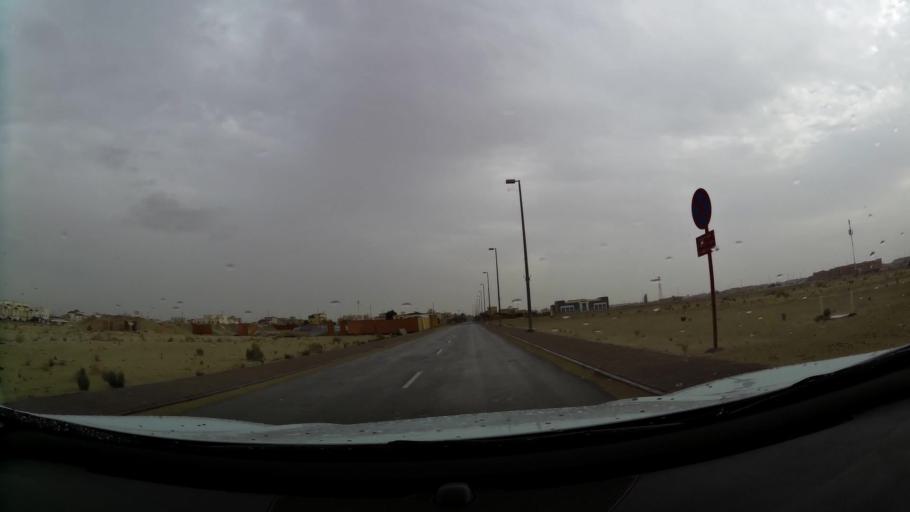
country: AE
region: Abu Dhabi
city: Abu Dhabi
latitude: 24.3683
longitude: 54.6330
